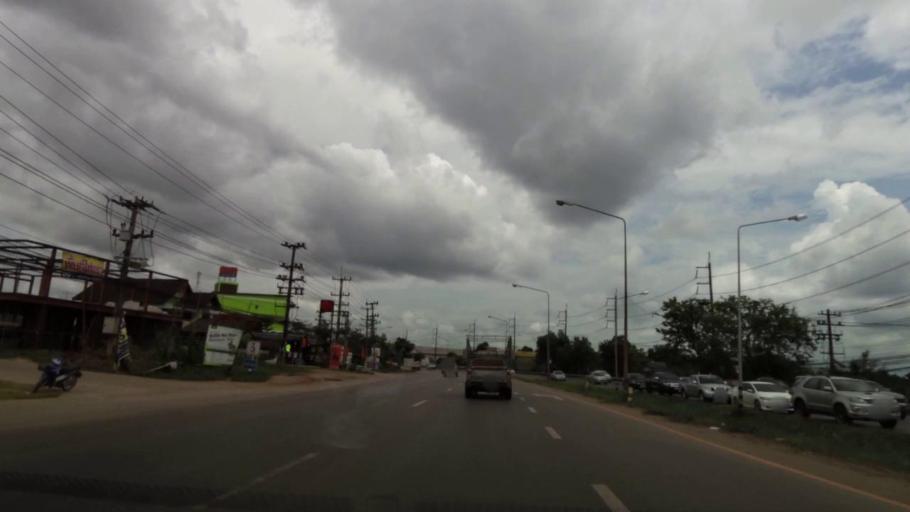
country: TH
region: Rayong
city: Klaeng
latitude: 12.7869
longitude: 101.6637
